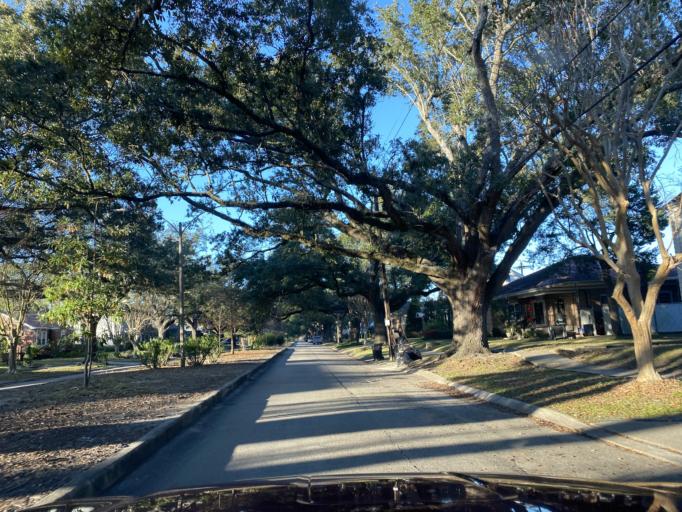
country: US
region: Louisiana
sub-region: Orleans Parish
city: New Orleans
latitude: 30.0059
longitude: -90.0552
